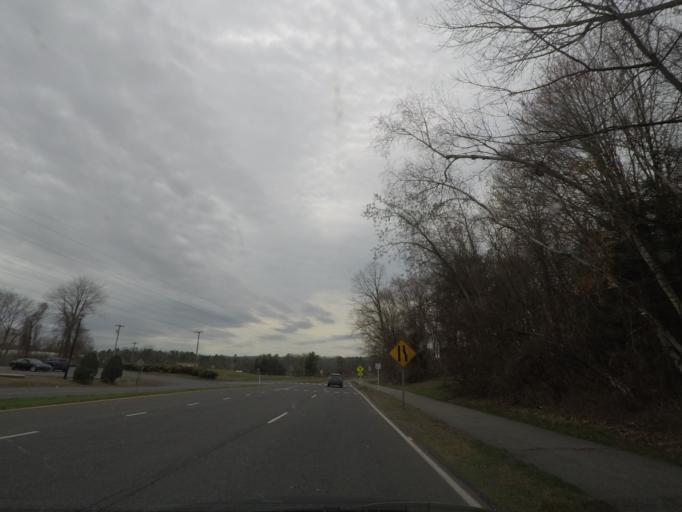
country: US
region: New York
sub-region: Albany County
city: Delmar
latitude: 42.6058
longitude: -73.8433
